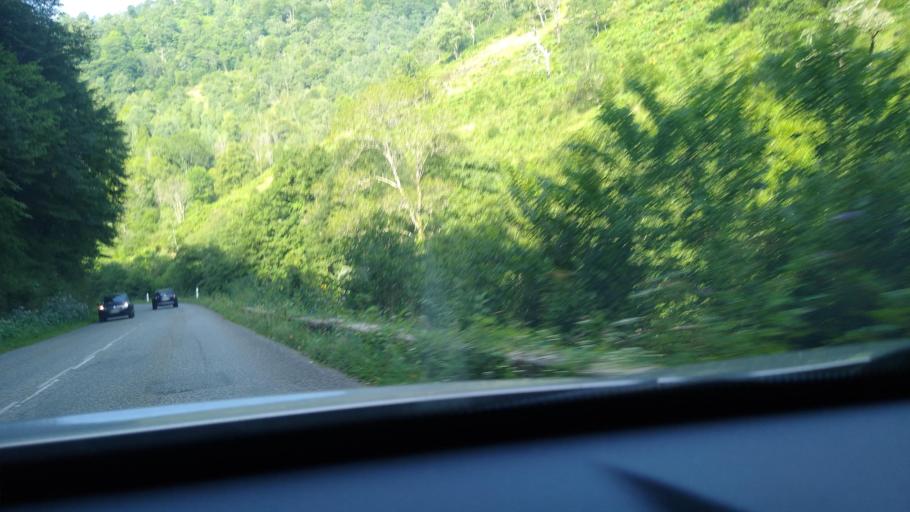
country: FR
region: Midi-Pyrenees
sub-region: Departement de l'Ariege
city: Saint-Girons
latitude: 42.8536
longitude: 1.1950
